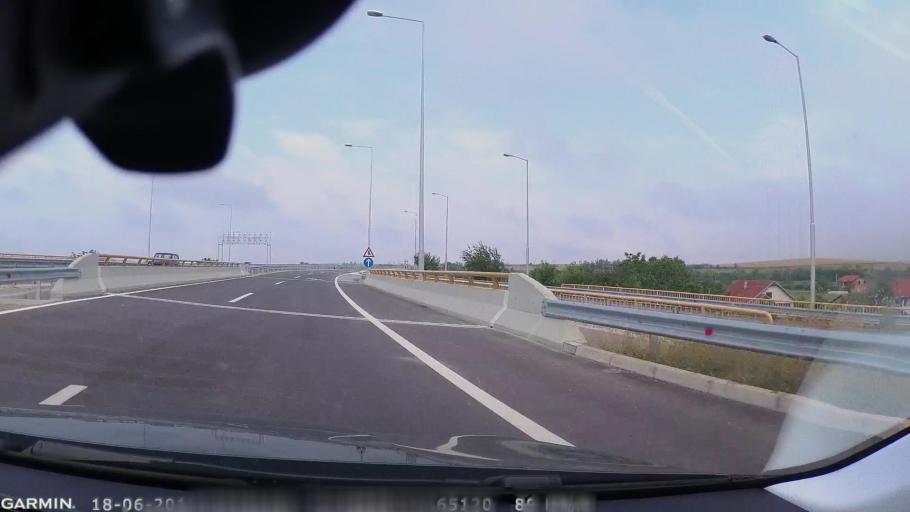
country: MK
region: Petrovec
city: Sredno Konjare
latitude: 41.9522
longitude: 21.7567
